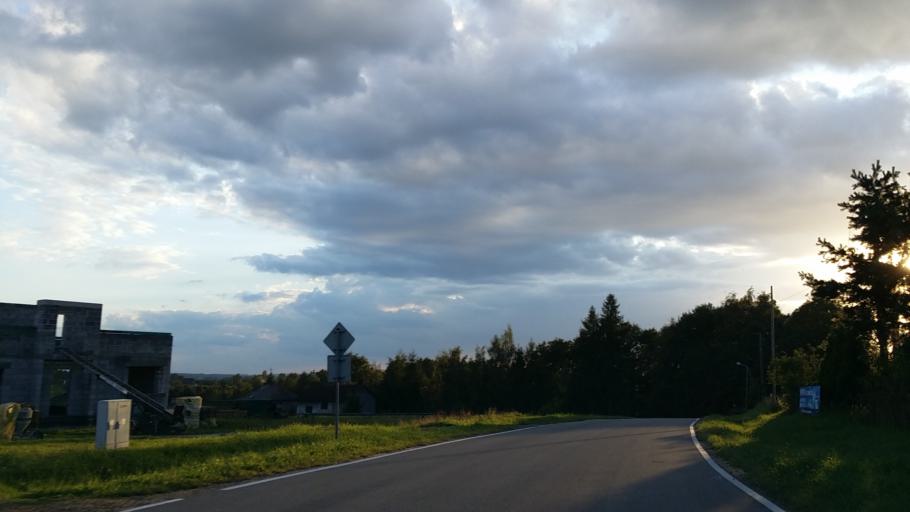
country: PL
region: Lesser Poland Voivodeship
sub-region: Powiat oswiecimski
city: Malec
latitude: 49.9236
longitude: 19.2491
